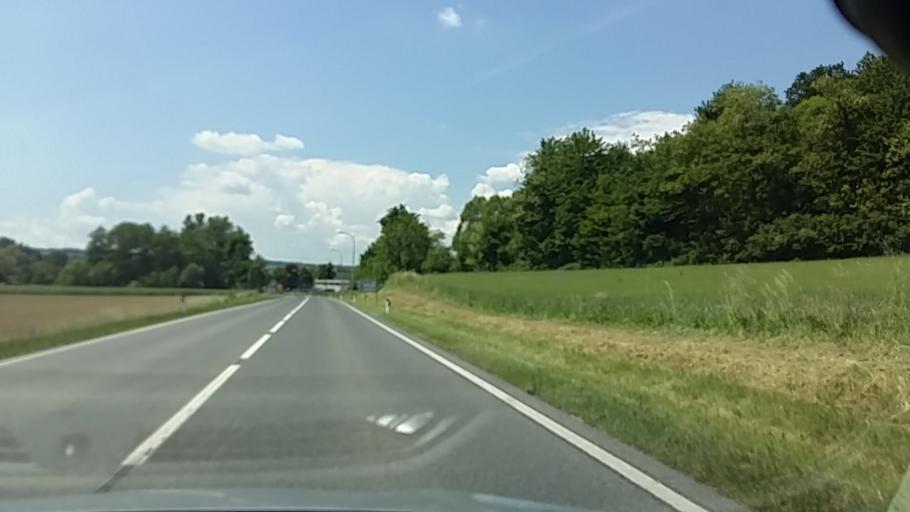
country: AT
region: Burgenland
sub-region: Politischer Bezirk Oberpullendorf
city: Piringsdorf
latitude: 47.4545
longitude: 16.4308
